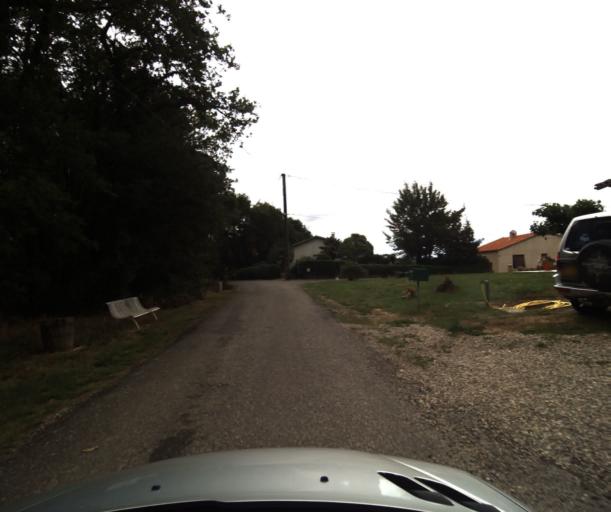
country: FR
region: Midi-Pyrenees
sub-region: Departement du Tarn-et-Garonne
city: Lavit
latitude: 43.9545
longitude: 0.9275
